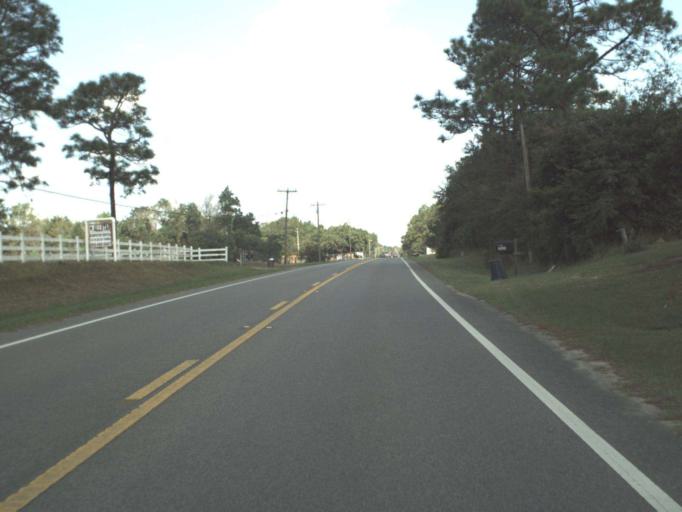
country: US
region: Florida
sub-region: Walton County
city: DeFuniak Springs
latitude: 30.7937
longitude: -86.1218
